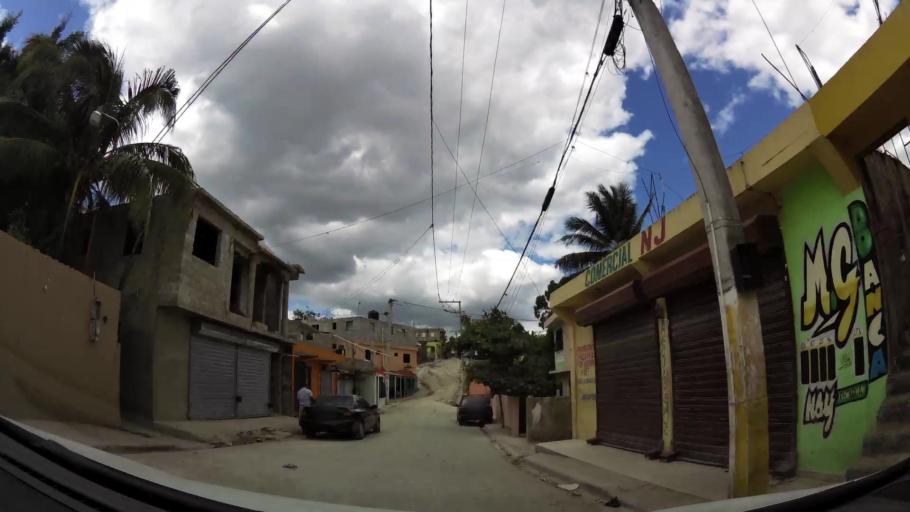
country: DO
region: Nacional
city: Ensanche Luperon
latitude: 18.5134
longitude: -69.9005
